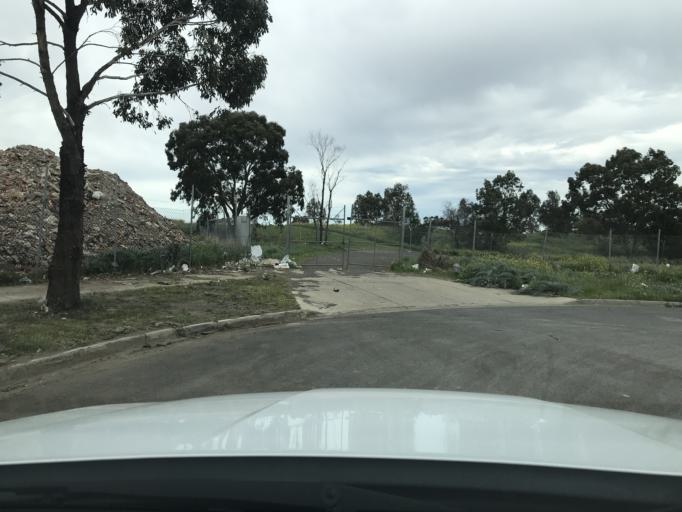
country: AU
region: Victoria
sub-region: Hume
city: Craigieburn
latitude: -37.6030
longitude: 144.9480
